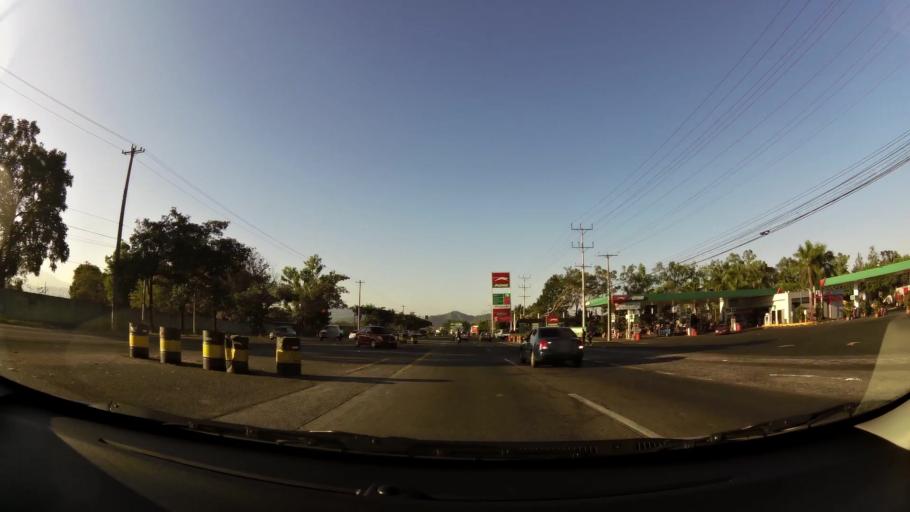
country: SV
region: La Libertad
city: Ciudad Arce
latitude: 13.7736
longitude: -89.3720
